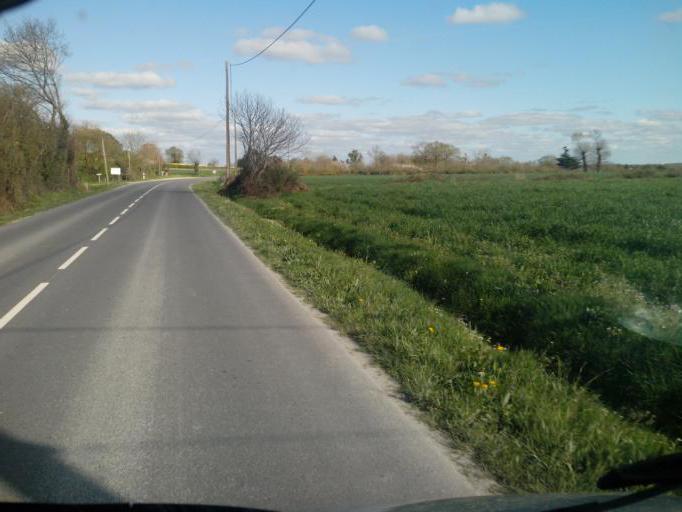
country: FR
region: Brittany
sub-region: Departement d'Ille-et-Vilaine
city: Maure-de-Bretagne
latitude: 47.8839
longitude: -1.9392
